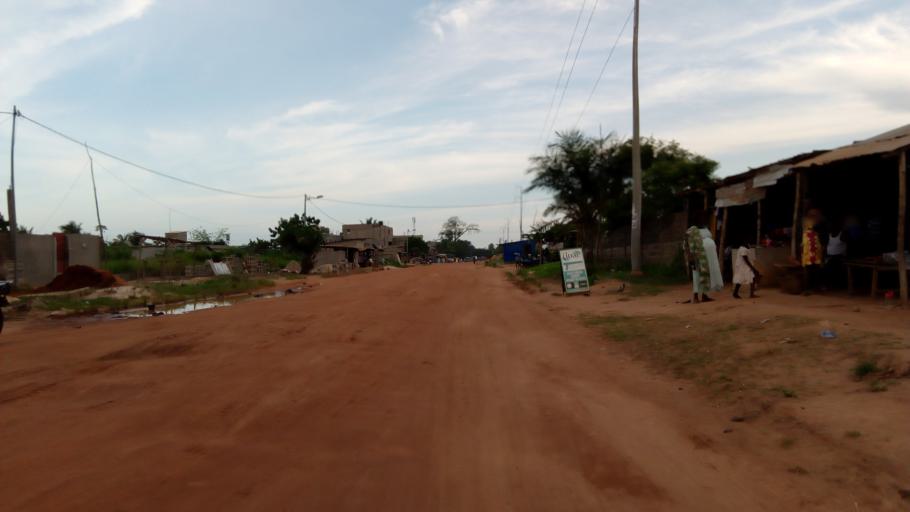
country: TG
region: Maritime
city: Lome
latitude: 6.2534
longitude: 1.1394
